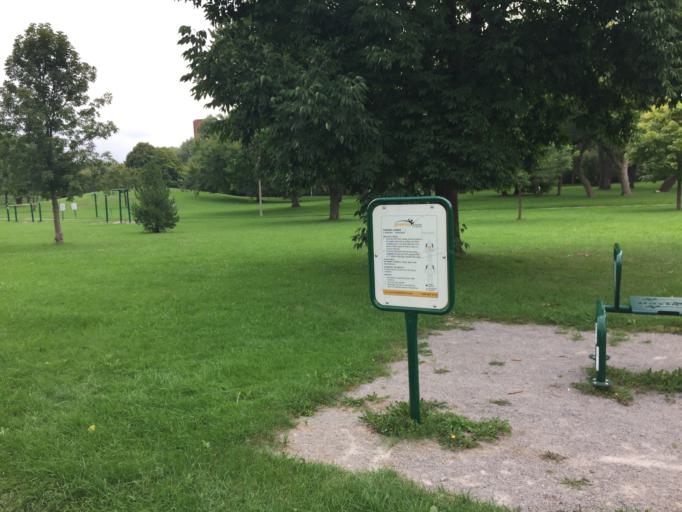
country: CA
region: Ontario
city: Oshawa
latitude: 43.8914
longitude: -78.8675
